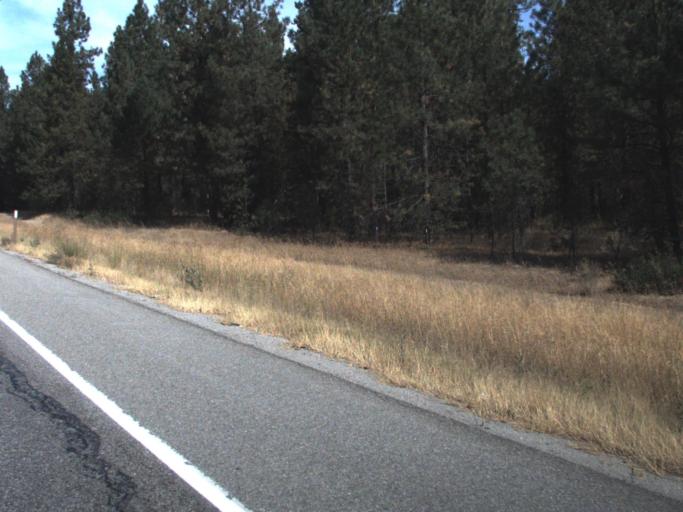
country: US
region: Washington
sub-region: Spokane County
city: Deer Park
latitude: 48.0636
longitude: -117.6223
